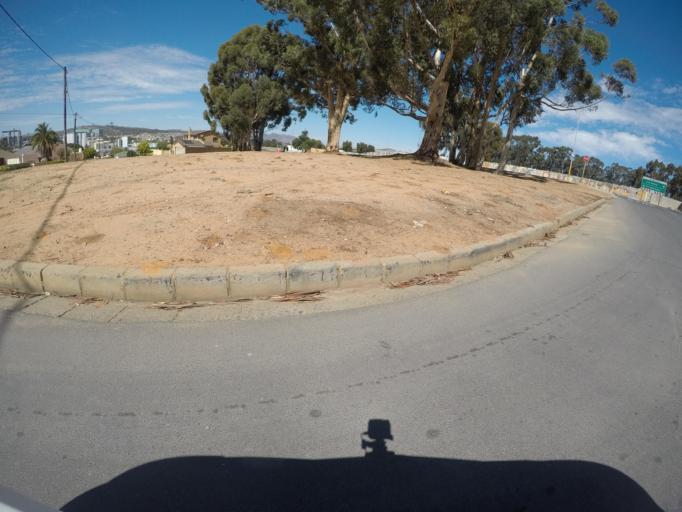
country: ZA
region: Western Cape
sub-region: West Coast District Municipality
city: Malmesbury
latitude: -33.4634
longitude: 18.7142
